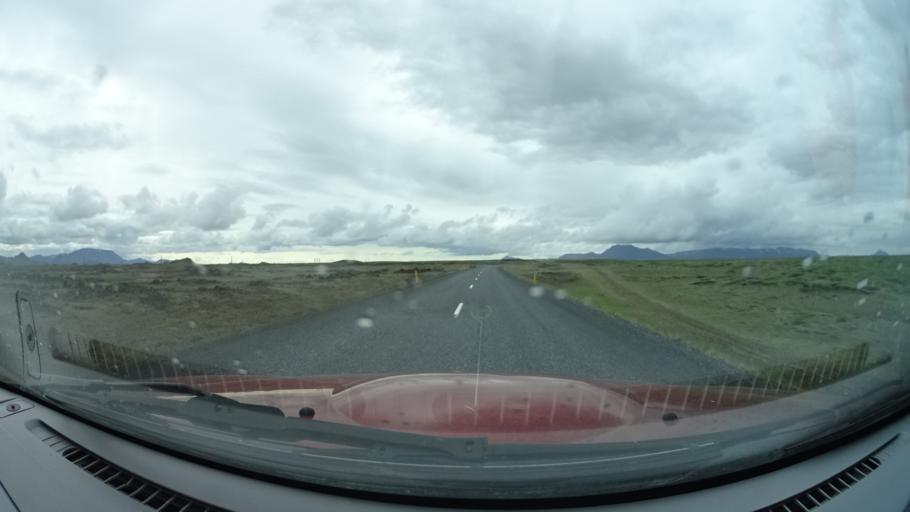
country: IS
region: Northeast
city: Laugar
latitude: 65.6546
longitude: -16.4467
